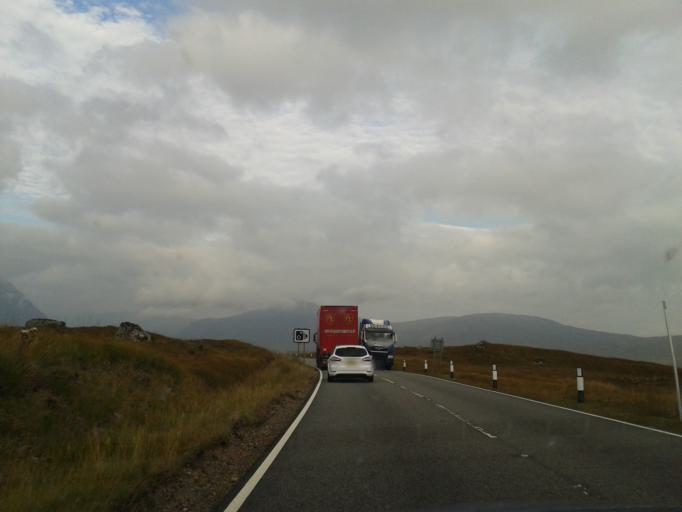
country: GB
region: Scotland
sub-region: Highland
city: Spean Bridge
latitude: 56.6272
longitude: -4.7690
